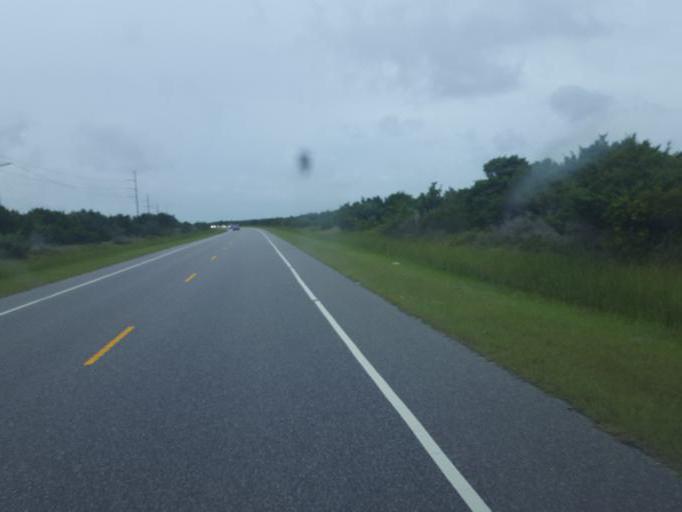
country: US
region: North Carolina
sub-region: Dare County
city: Buxton
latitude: 35.4033
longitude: -75.4894
